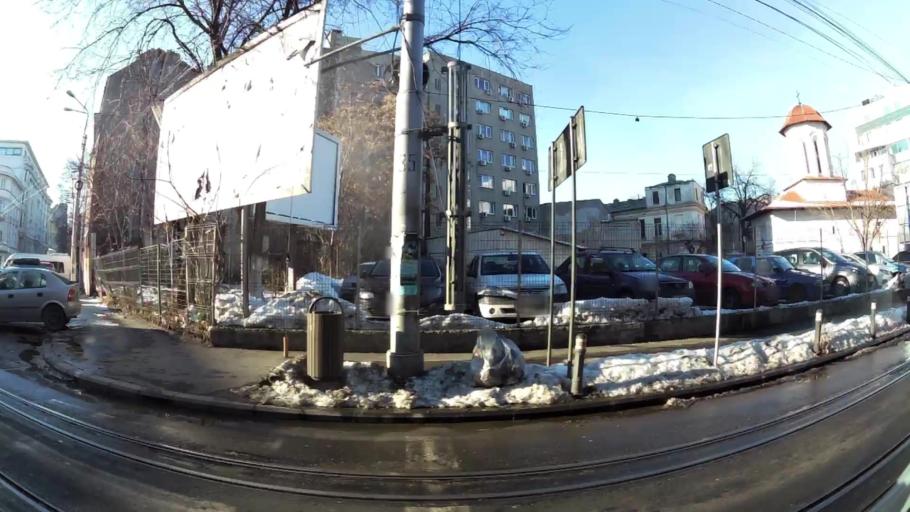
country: RO
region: Bucuresti
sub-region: Municipiul Bucuresti
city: Bucharest
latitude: 44.4325
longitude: 26.1063
